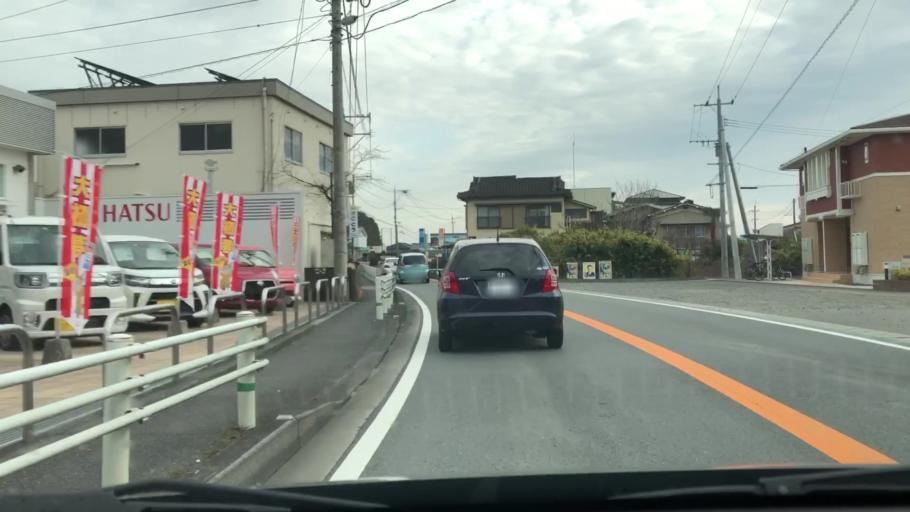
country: JP
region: Oita
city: Takedamachi
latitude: 32.9886
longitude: 131.6052
